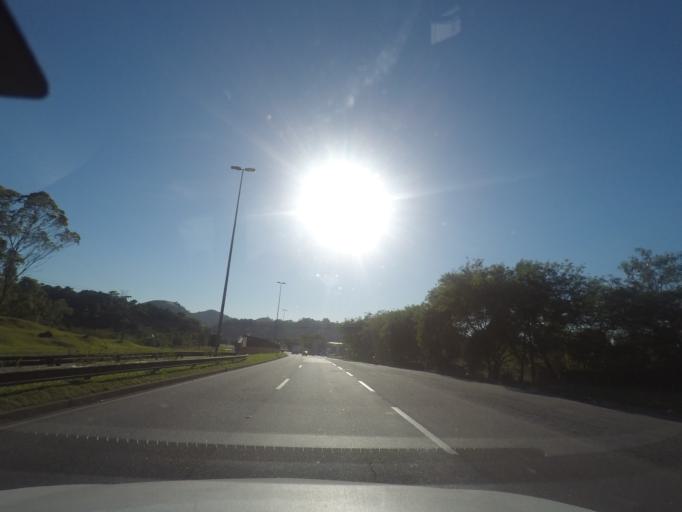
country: BR
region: Rio de Janeiro
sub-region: Petropolis
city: Petropolis
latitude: -22.6571
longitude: -43.1336
